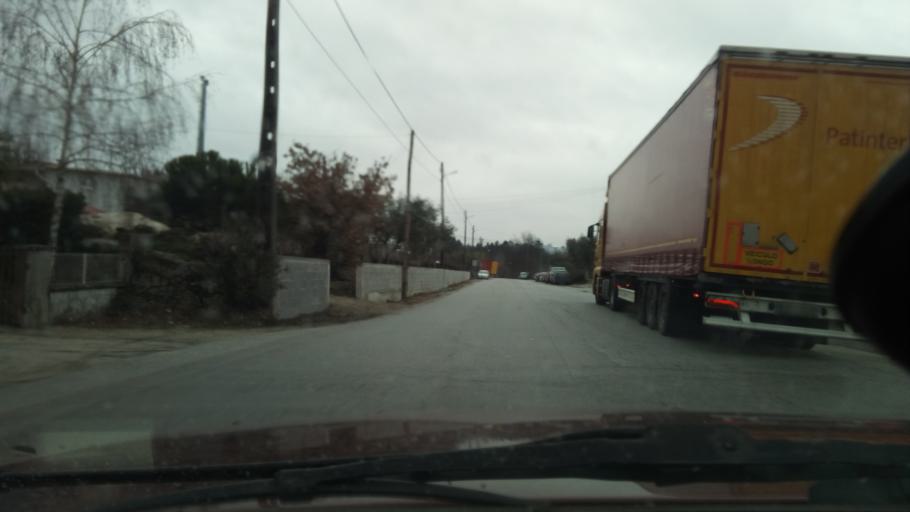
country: PT
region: Viseu
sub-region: Mangualde
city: Mangualde
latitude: 40.6198
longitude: -7.7990
